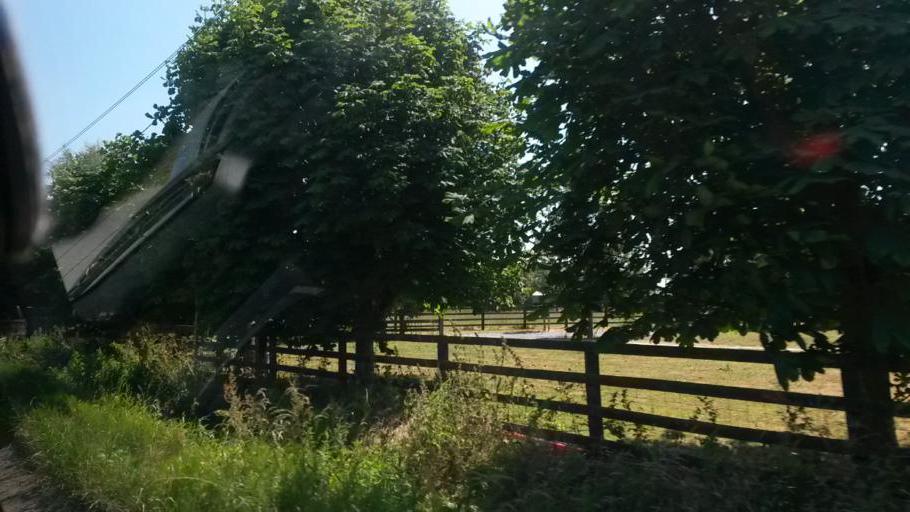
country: IE
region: Leinster
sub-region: An Mhi
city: Ashbourne
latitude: 53.5284
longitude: -6.3031
